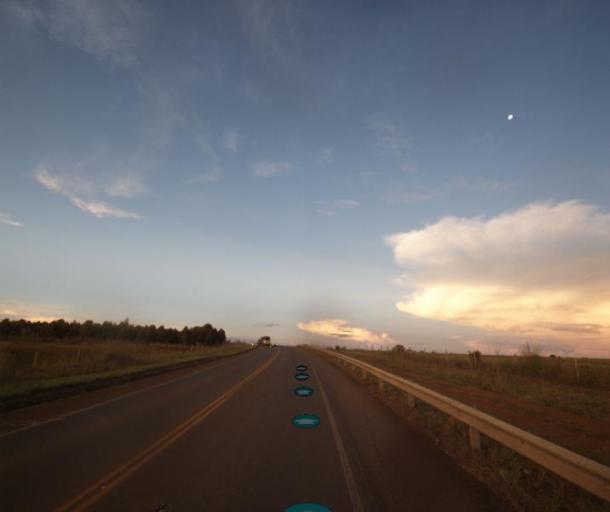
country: BR
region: Goias
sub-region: Pirenopolis
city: Pirenopolis
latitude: -16.0222
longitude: -48.8393
